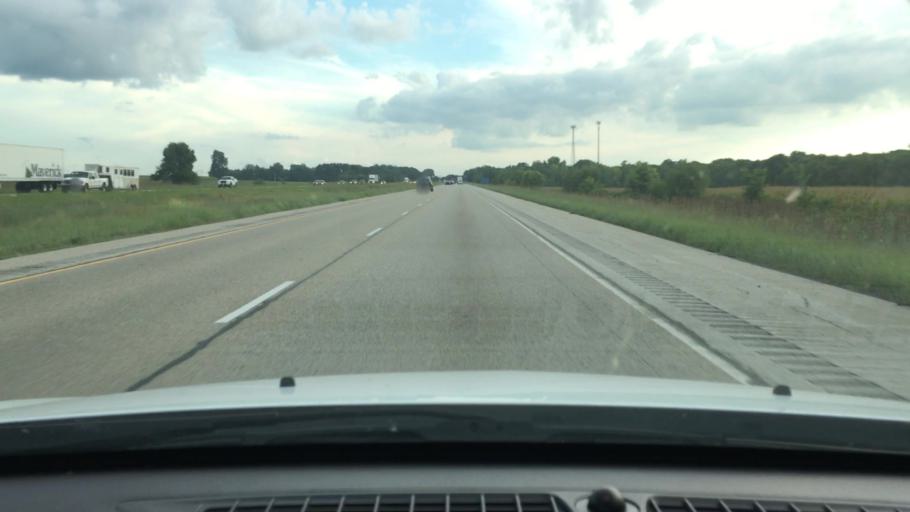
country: US
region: Illinois
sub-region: McLean County
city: Twin Grove
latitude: 40.3694
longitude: -89.1007
